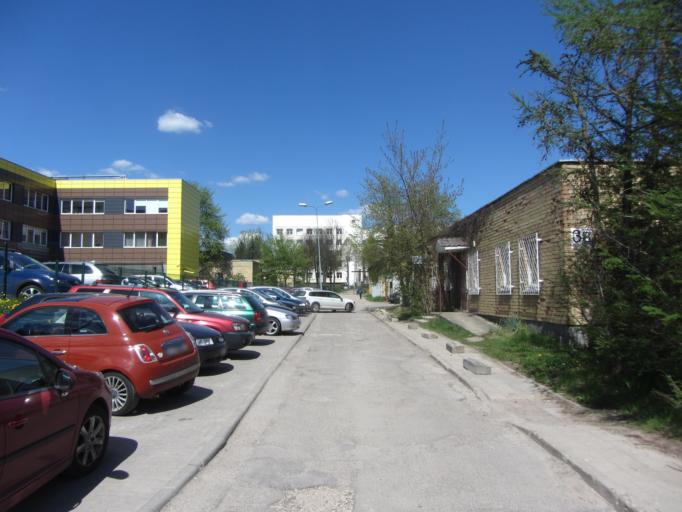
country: LT
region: Vilnius County
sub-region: Vilnius
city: Fabijoniskes
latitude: 54.7530
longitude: 25.2827
